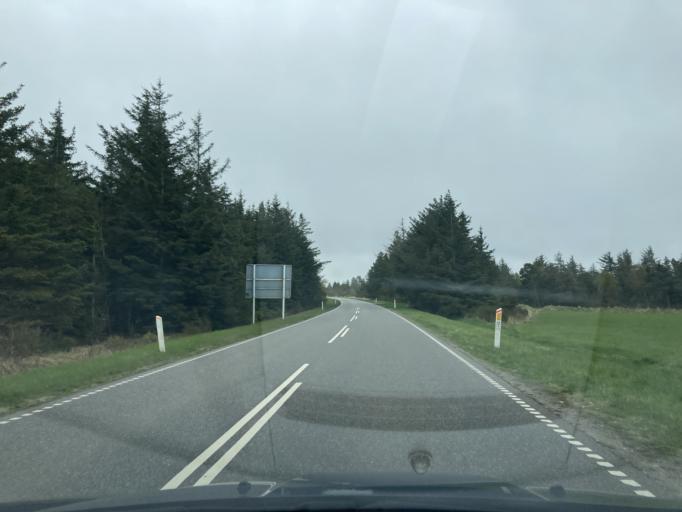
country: DK
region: North Denmark
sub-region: Thisted Kommune
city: Hurup
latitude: 56.9172
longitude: 8.3732
